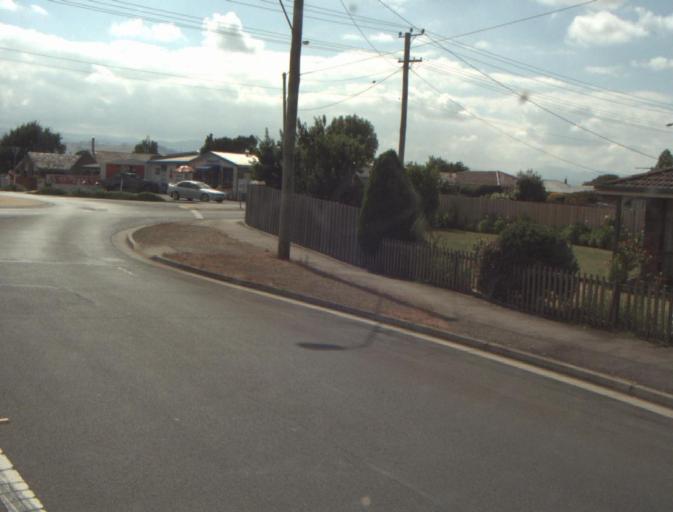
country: AU
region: Tasmania
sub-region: Launceston
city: Newstead
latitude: -41.4693
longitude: 147.1775
